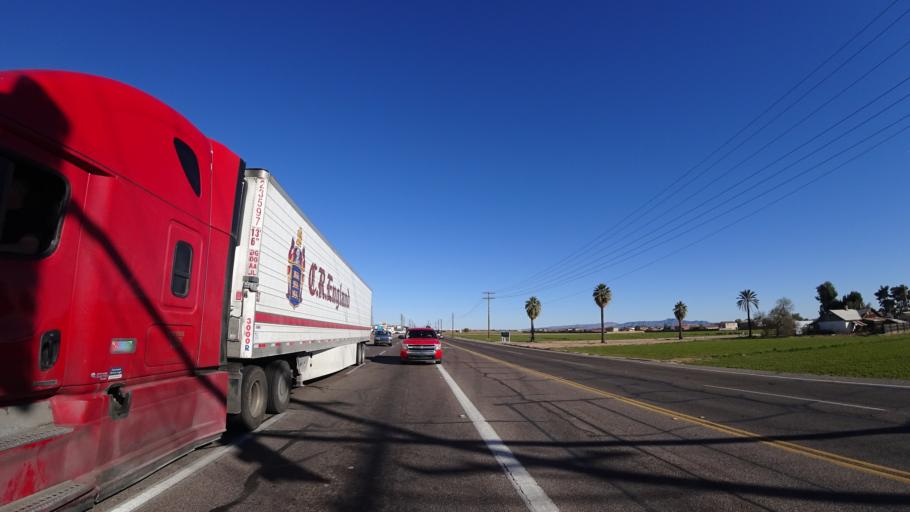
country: US
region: Arizona
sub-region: Maricopa County
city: Tolleson
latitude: 33.4354
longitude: -112.2895
